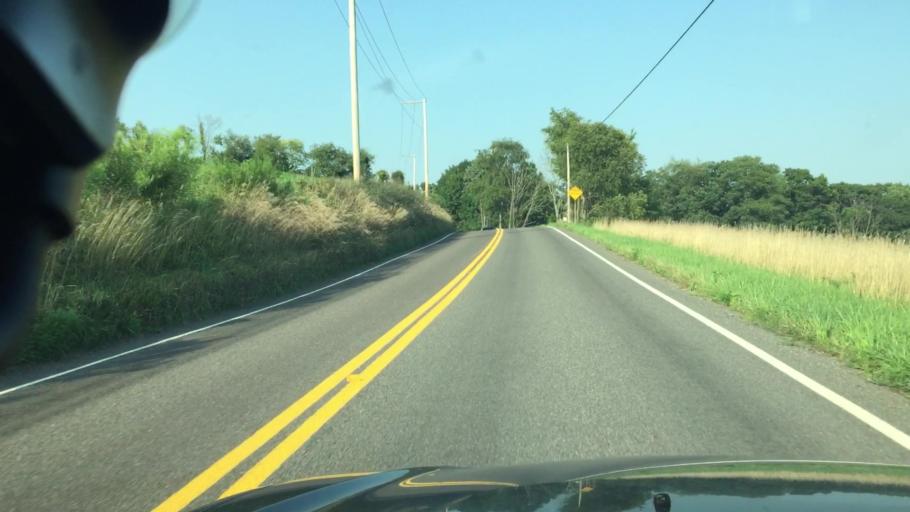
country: US
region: Pennsylvania
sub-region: Columbia County
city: Mifflinville
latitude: 40.9952
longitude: -76.3301
